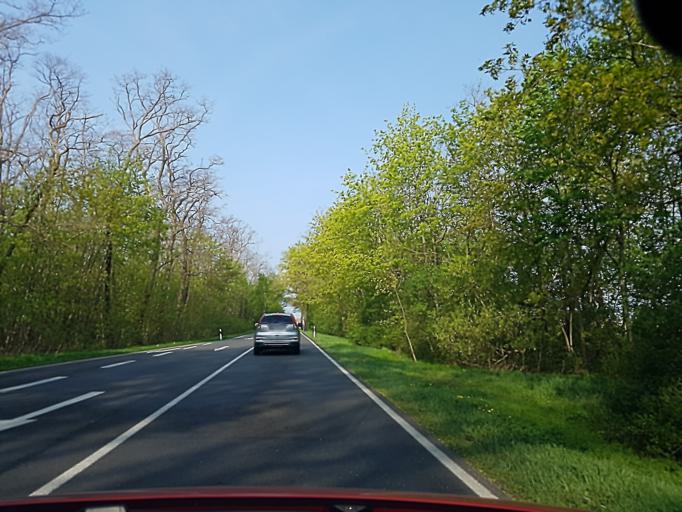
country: DE
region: Saxony
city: Beilrode
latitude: 51.5806
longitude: 13.0530
